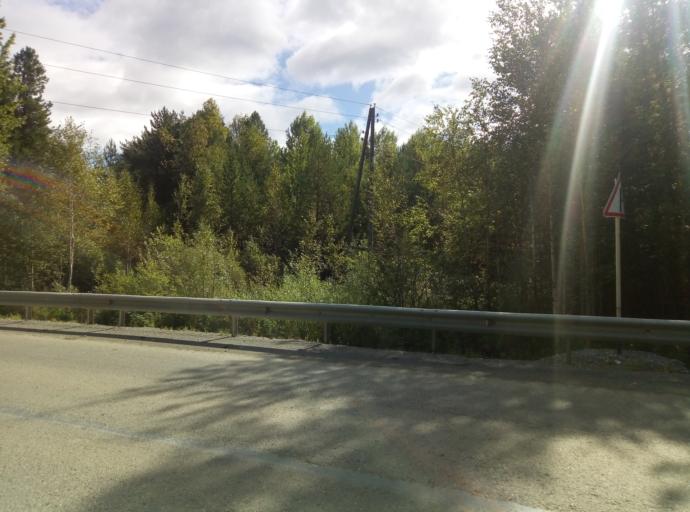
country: RU
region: Sverdlovsk
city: Karpinsk
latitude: 59.7147
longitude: 59.9428
